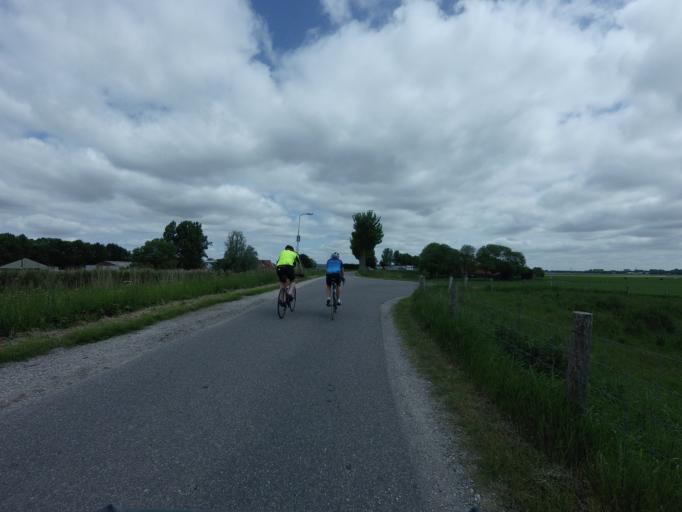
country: NL
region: North Holland
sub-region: Gemeente Beemster
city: Halfweg
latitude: 52.5458
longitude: 4.8438
